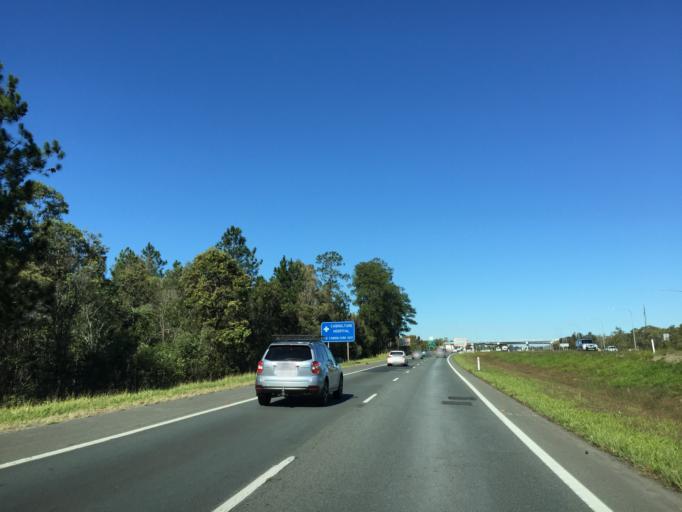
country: AU
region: Queensland
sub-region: Moreton Bay
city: Caboolture
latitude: -27.0660
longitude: 152.9777
